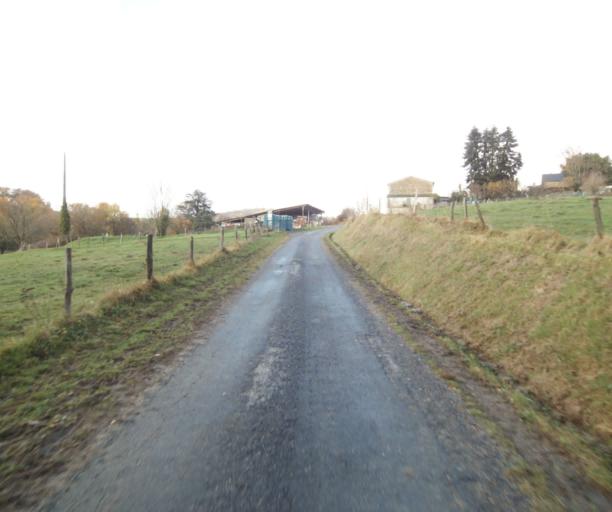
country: FR
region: Limousin
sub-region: Departement de la Correze
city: Cornil
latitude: 45.2181
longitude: 1.6708
